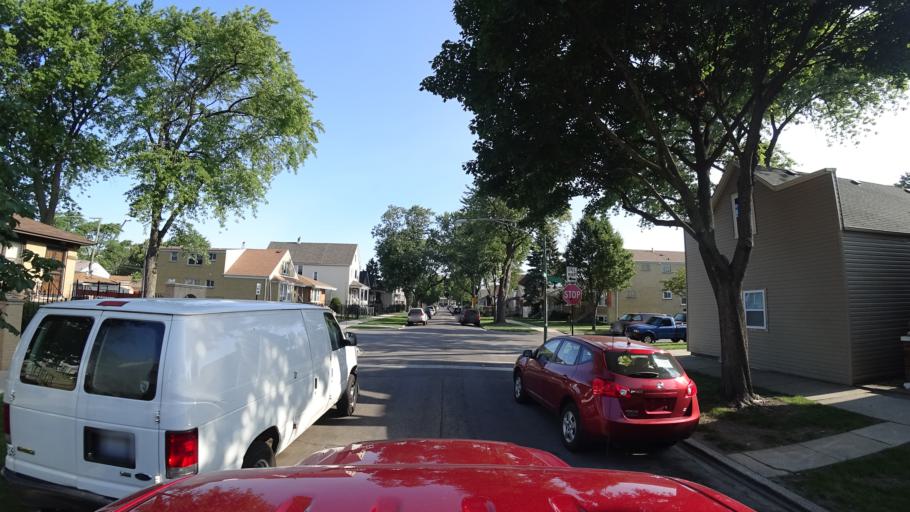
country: US
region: Illinois
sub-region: Cook County
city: Cicero
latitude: 41.7986
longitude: -87.7099
